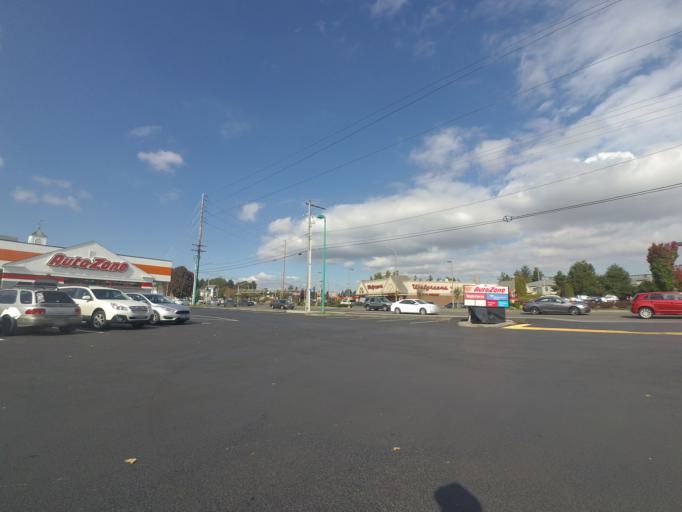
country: US
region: Washington
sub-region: Pierce County
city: Lakewood
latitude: 47.1706
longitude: -122.5181
